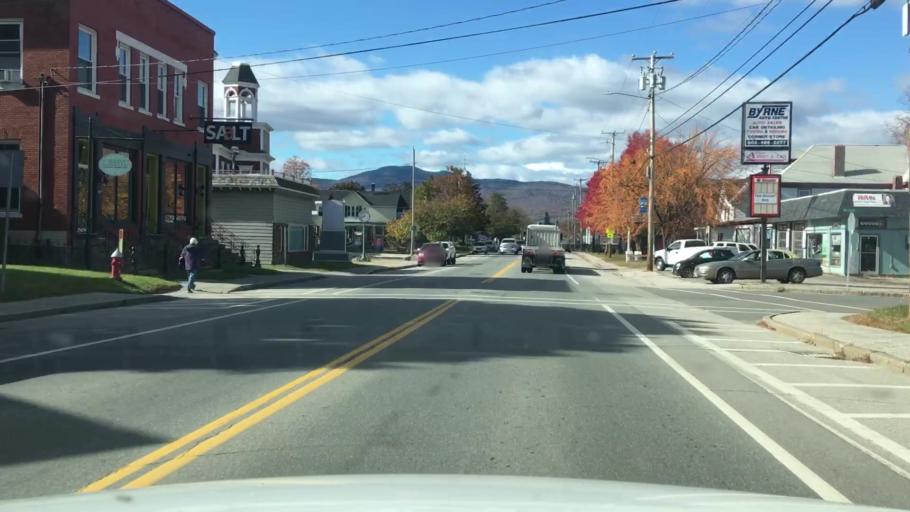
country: US
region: New Hampshire
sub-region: Coos County
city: Gorham
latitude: 44.3891
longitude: -71.1770
